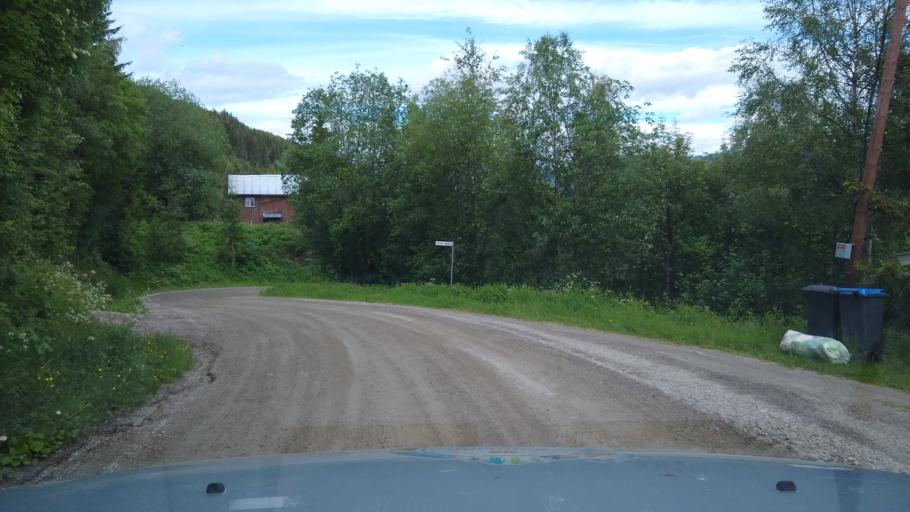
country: NO
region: Oppland
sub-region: Ringebu
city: Ringebu
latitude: 61.5087
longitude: 10.1354
